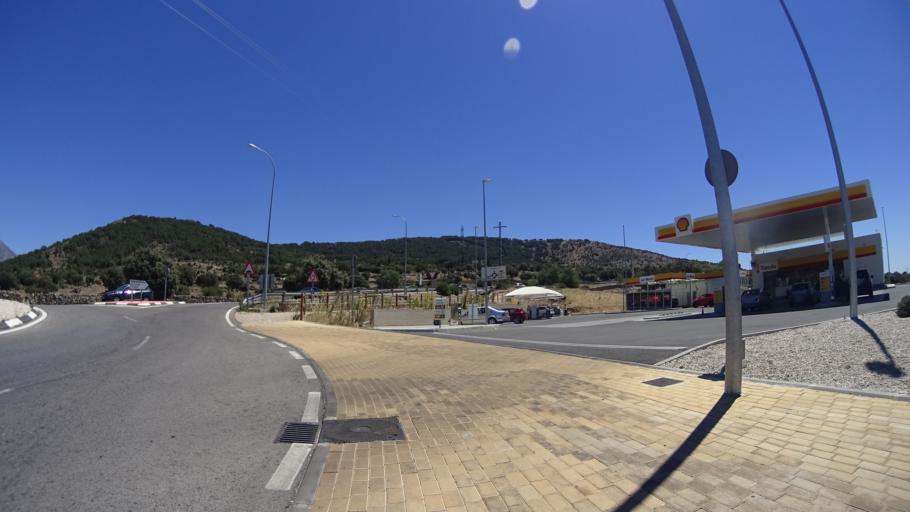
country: ES
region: Madrid
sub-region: Provincia de Madrid
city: Collado Mediano
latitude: 40.6861
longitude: -4.0156
